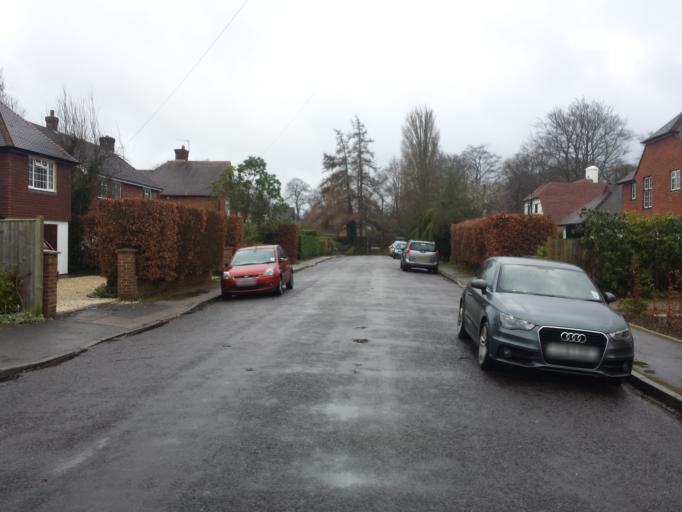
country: GB
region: England
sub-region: Surrey
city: Godalming
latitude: 51.1796
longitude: -0.6090
